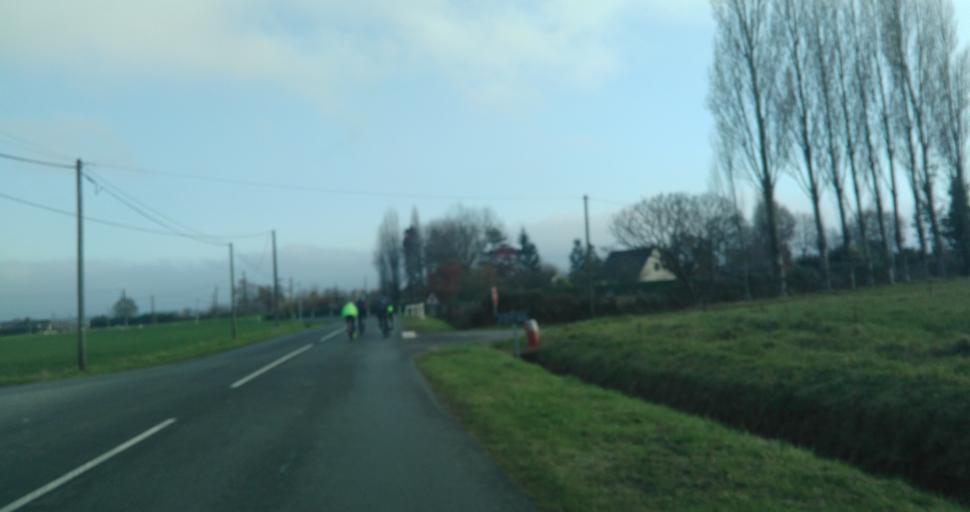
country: FR
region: Brittany
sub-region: Departement d'Ille-et-Vilaine
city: Saint-Meen-le-Grand
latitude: 48.1809
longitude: -2.1559
